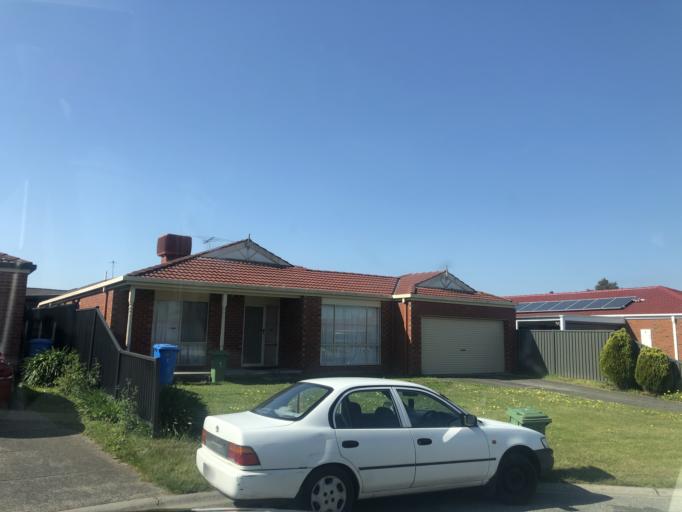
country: AU
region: Victoria
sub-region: Casey
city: Lynbrook
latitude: -38.0476
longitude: 145.2711
